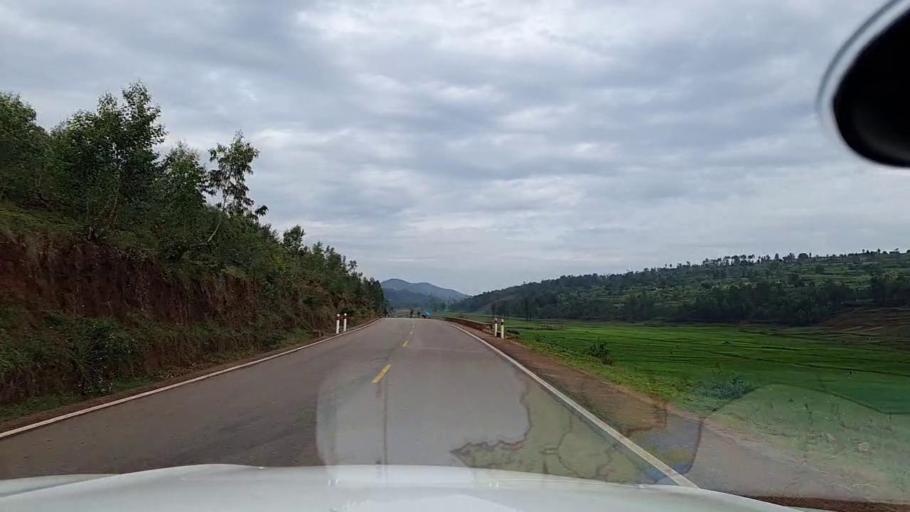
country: RW
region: Southern Province
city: Butare
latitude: -2.5692
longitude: 29.7297
